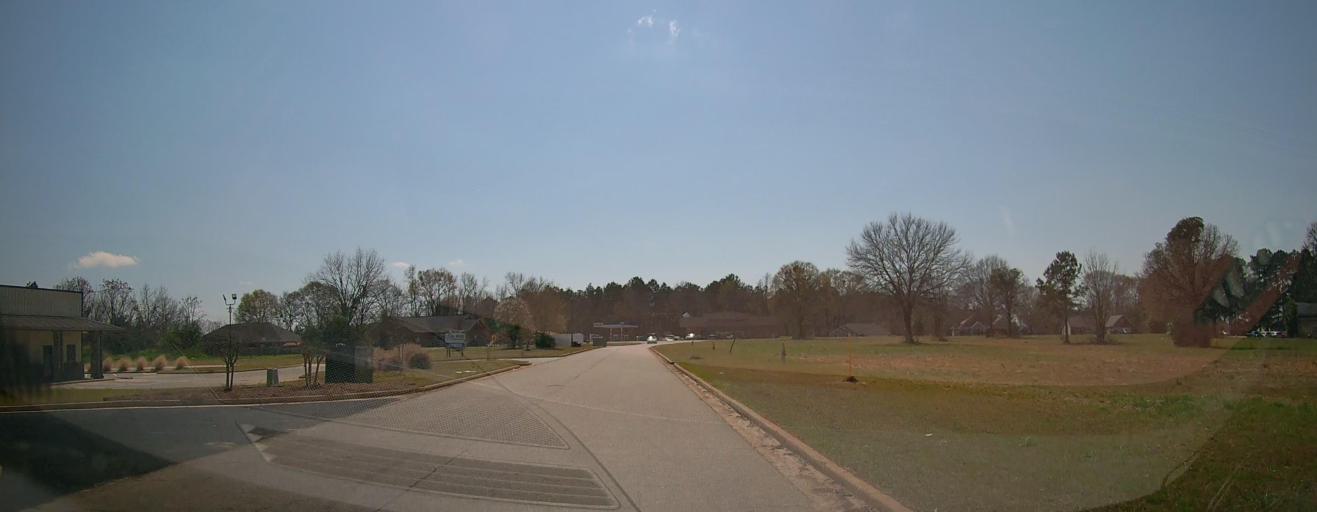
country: US
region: Georgia
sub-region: Houston County
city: Centerville
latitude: 32.6101
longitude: -83.6816
